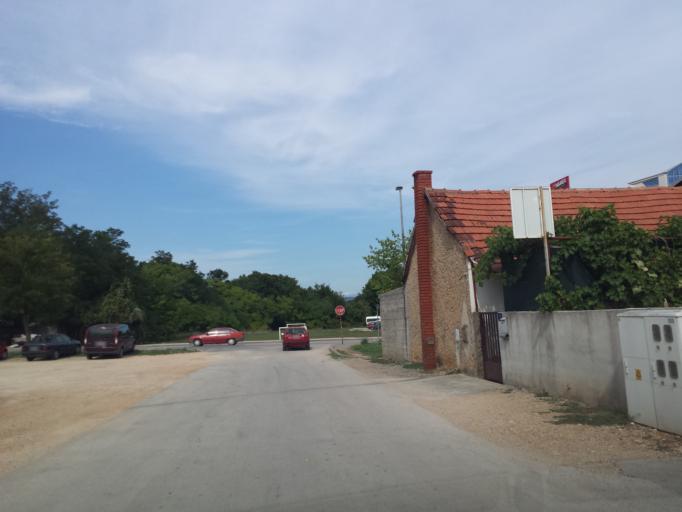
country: BA
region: Federation of Bosnia and Herzegovina
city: Citluk
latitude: 43.1956
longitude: 17.6750
